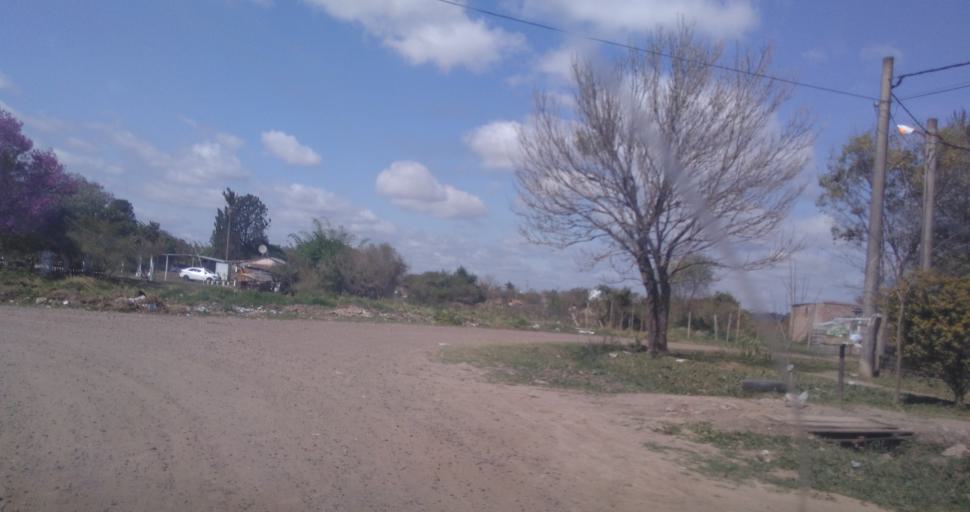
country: AR
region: Chaco
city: Fontana
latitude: -27.4317
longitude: -59.0326
